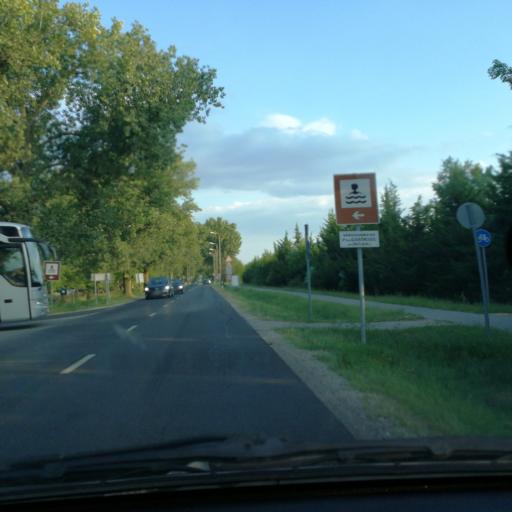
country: HU
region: Bacs-Kiskun
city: Kiskunmajsa
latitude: 46.5244
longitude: 19.7446
